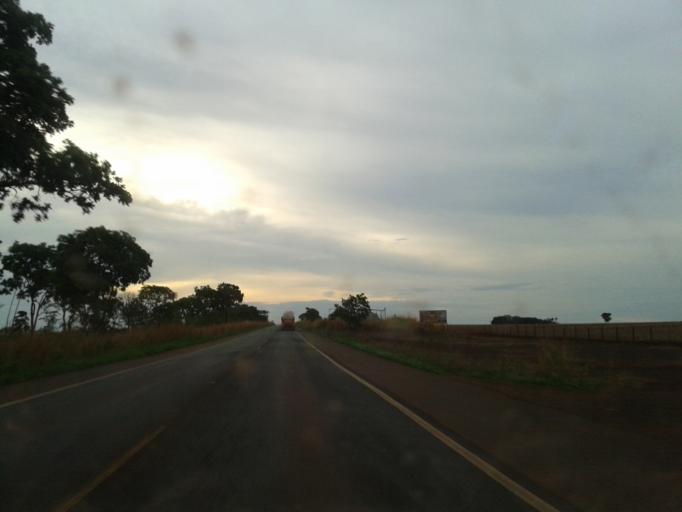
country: BR
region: Goias
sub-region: Santa Helena De Goias
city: Santa Helena de Goias
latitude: -17.9392
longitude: -50.5312
